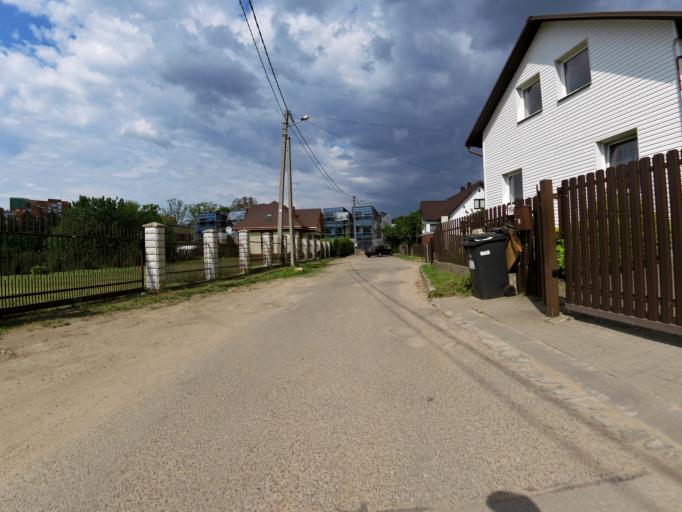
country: LT
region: Vilnius County
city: Seskine
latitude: 54.7249
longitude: 25.2757
